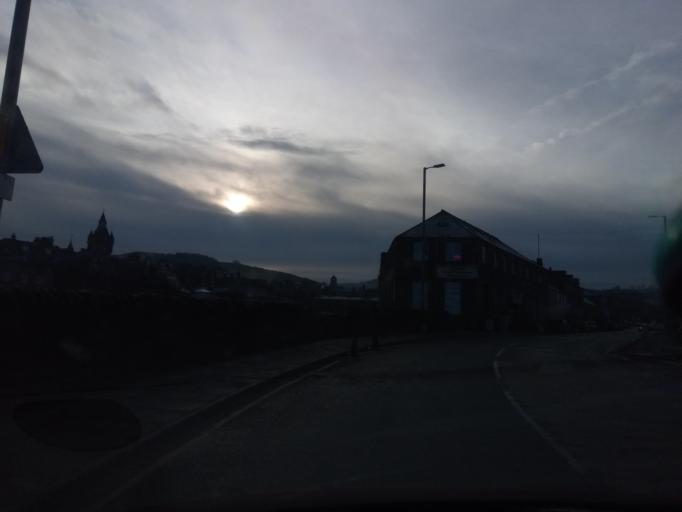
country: GB
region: Scotland
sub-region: The Scottish Borders
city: Hawick
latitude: 55.4247
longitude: -2.7881
